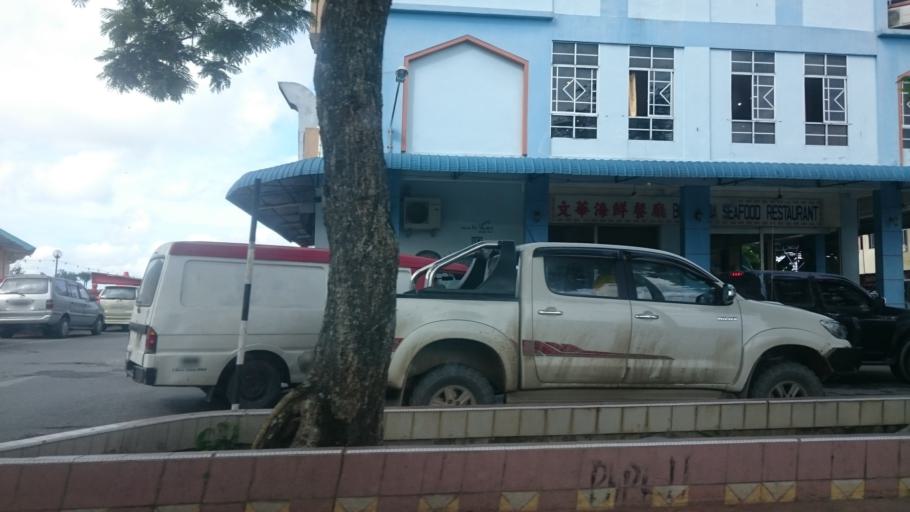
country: MY
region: Sarawak
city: Limbang
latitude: 4.7552
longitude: 115.0085
